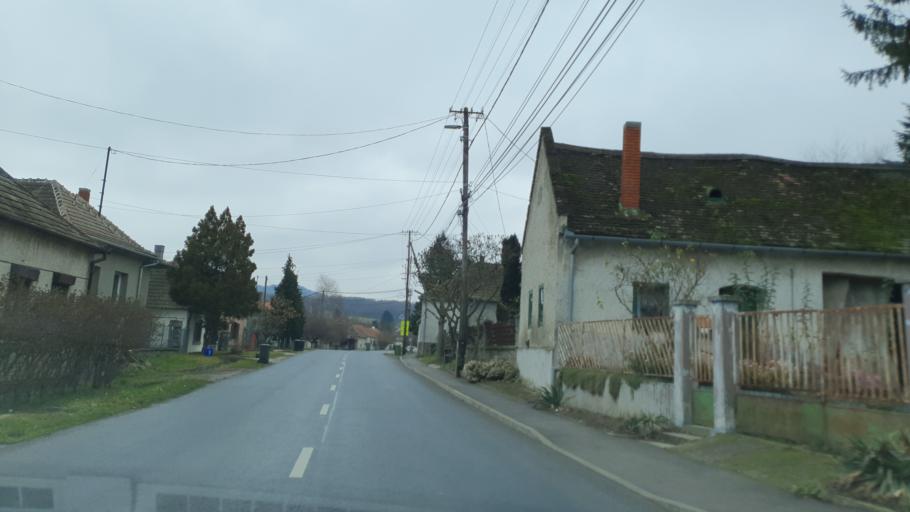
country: HU
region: Veszprem
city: Sumeg
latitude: 46.9309
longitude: 17.2444
